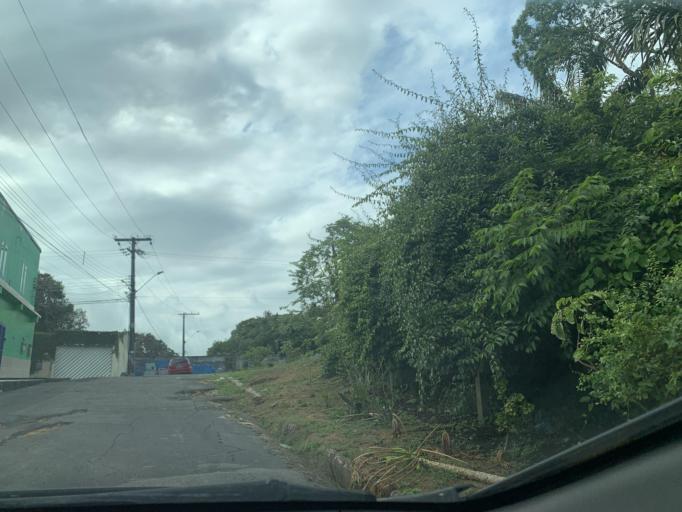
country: BR
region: Amazonas
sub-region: Manaus
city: Manaus
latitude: -3.0875
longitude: -59.9738
